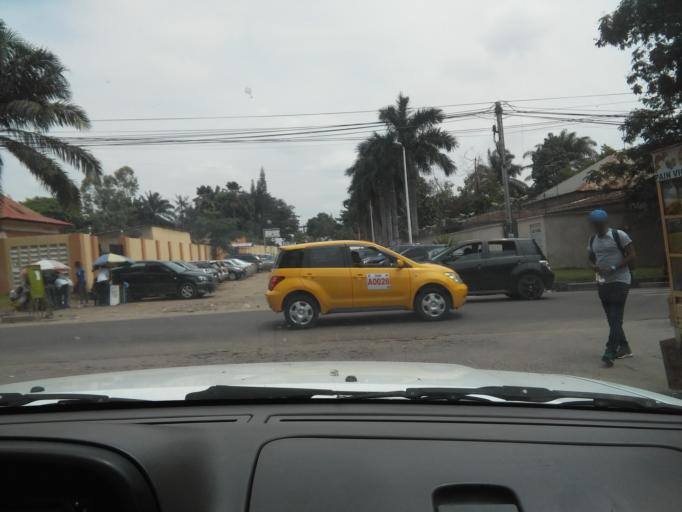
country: CD
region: Kinshasa
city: Kinshasa
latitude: -4.3079
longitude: 15.2911
